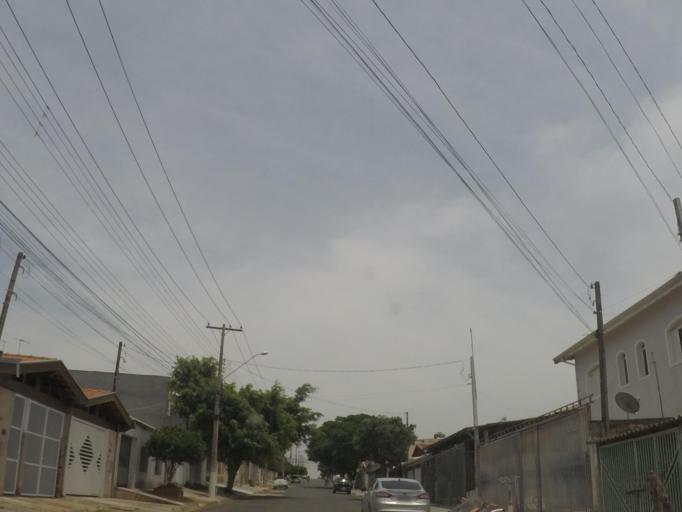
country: BR
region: Sao Paulo
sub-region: Hortolandia
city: Hortolandia
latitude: -22.8488
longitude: -47.1951
